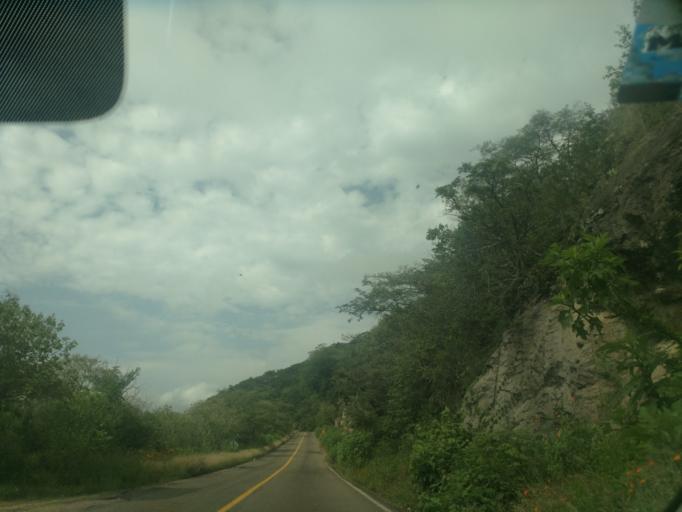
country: MX
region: Jalisco
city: El Salto
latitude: 20.3672
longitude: -104.5760
